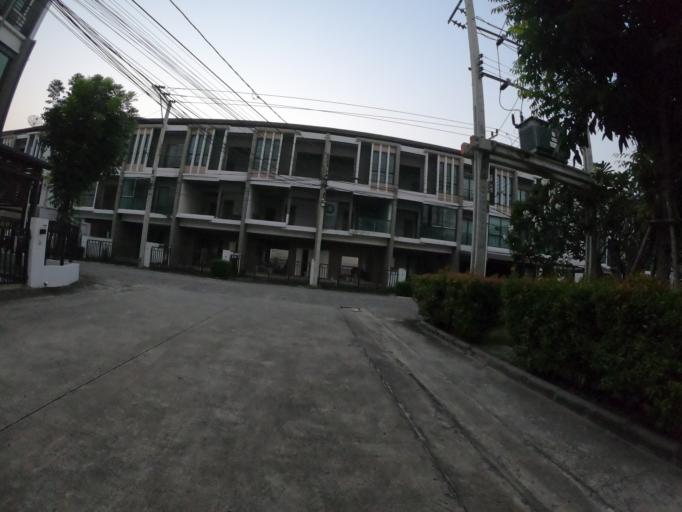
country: TH
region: Bangkok
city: Lat Phrao
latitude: 13.8279
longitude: 100.6220
